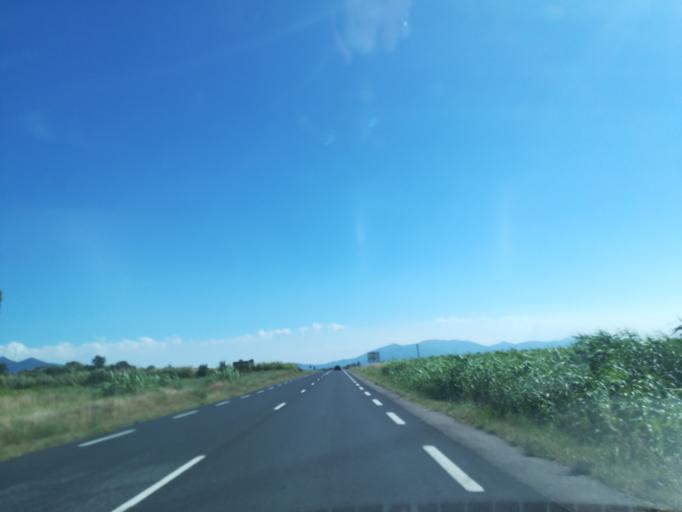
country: FR
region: Languedoc-Roussillon
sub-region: Departement des Pyrenees-Orientales
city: Villemolaque
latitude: 42.5922
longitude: 2.8532
